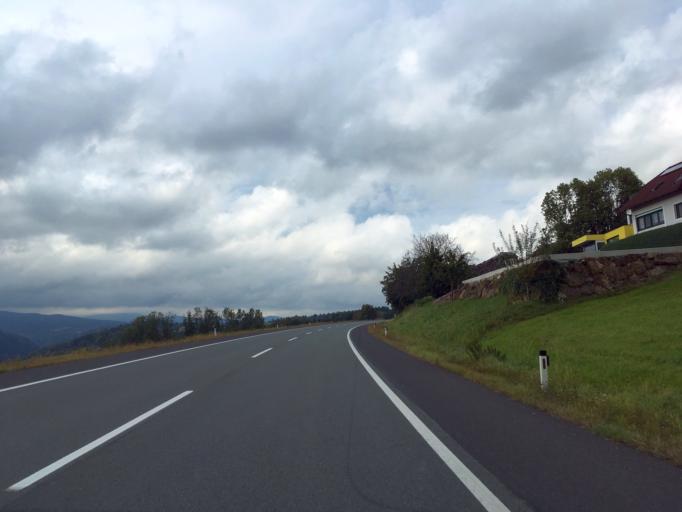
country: AT
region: Styria
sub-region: Politischer Bezirk Hartberg-Fuerstenfeld
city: Pinggau
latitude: 47.4433
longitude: 16.0760
